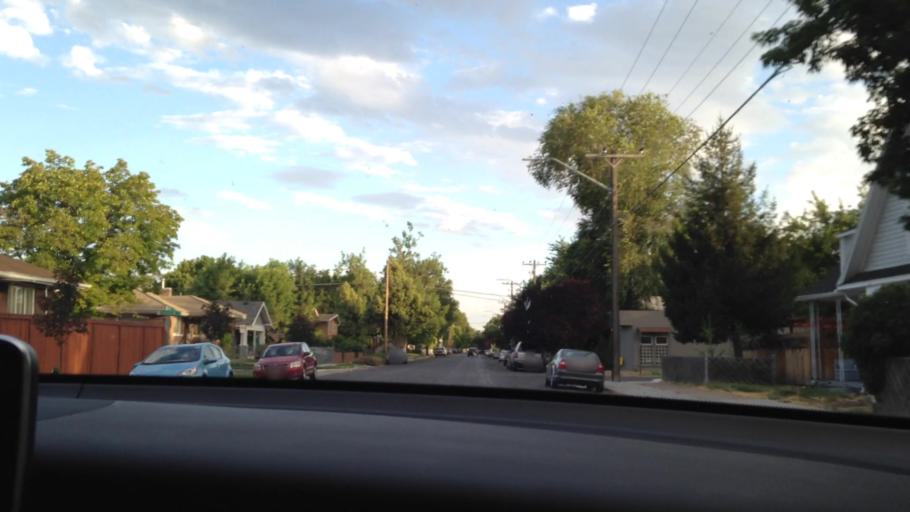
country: US
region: Utah
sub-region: Salt Lake County
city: South Salt Lake
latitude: 40.7319
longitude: -111.8797
